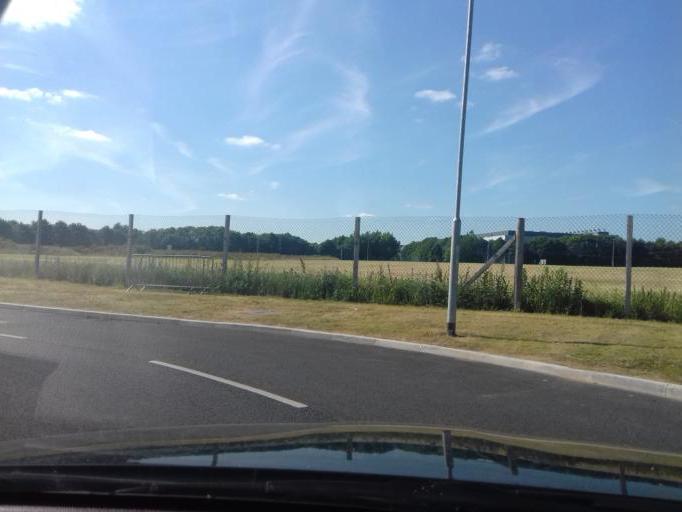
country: IE
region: Leinster
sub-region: Fingal County
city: Blanchardstown
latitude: 53.3996
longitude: -6.3607
